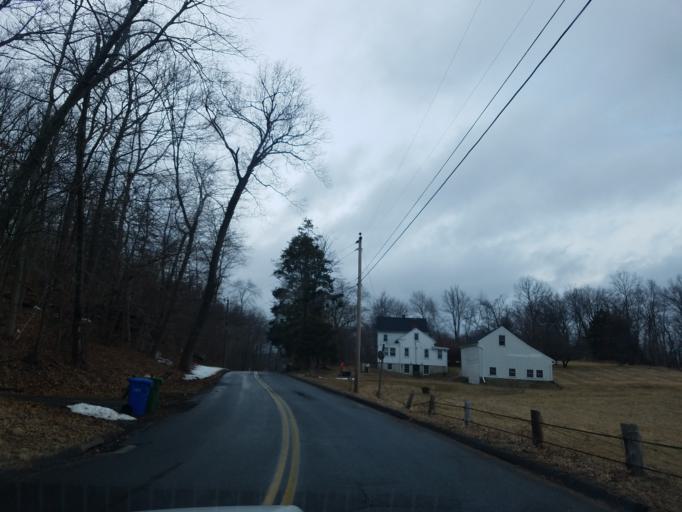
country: US
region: Connecticut
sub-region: Hartford County
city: Glastonbury Center
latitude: 41.6634
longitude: -72.5617
